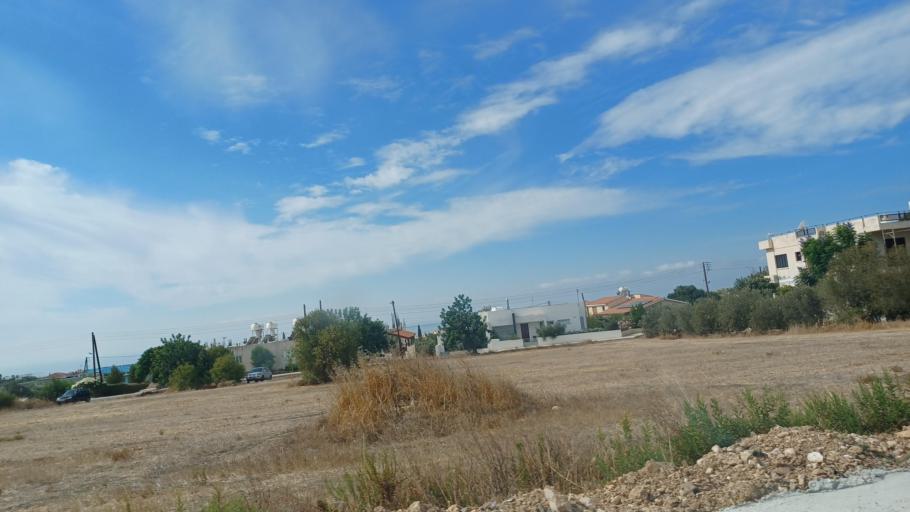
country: CY
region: Pafos
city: Mesogi
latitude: 34.8019
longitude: 32.4470
